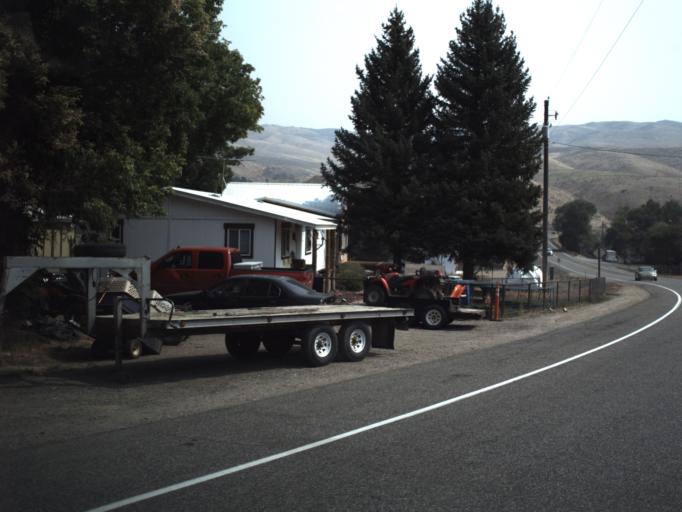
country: US
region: Utah
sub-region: Summit County
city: Coalville
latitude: 41.0142
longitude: -111.4950
